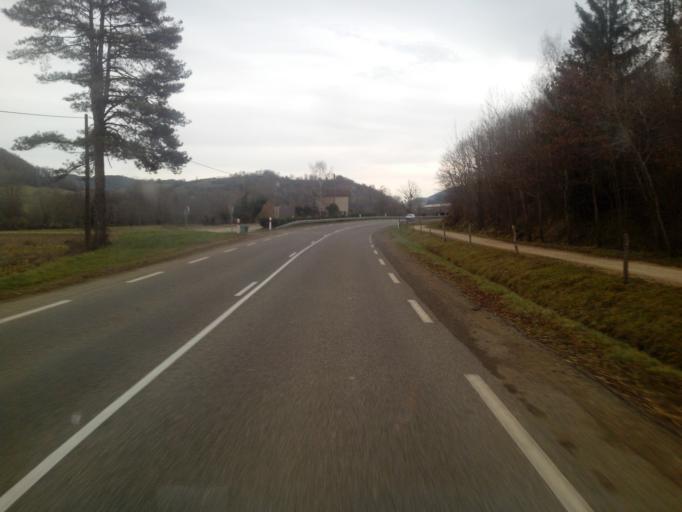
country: FR
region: Midi-Pyrenees
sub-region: Departement de l'Ariege
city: Foix
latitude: 43.0171
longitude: 1.4018
